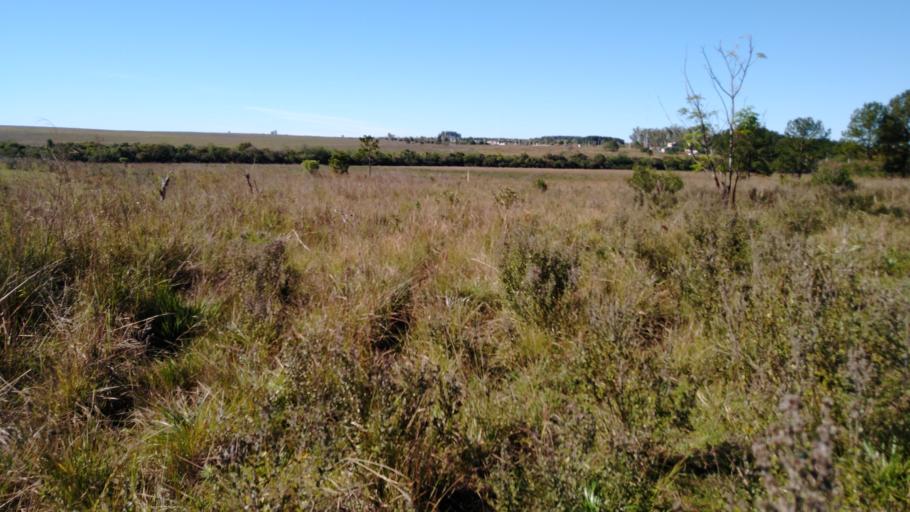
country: PY
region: Itapua
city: San Juan del Parana
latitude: -27.4537
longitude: -56.0565
